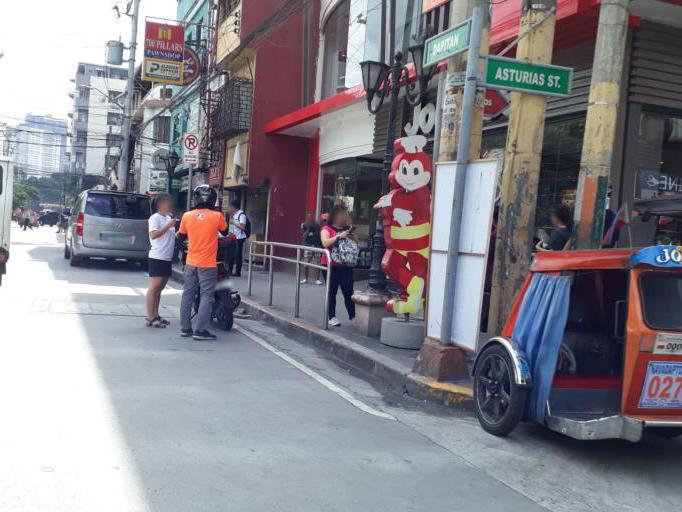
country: PH
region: Metro Manila
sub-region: City of Manila
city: Manila
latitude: 14.6116
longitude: 120.9883
